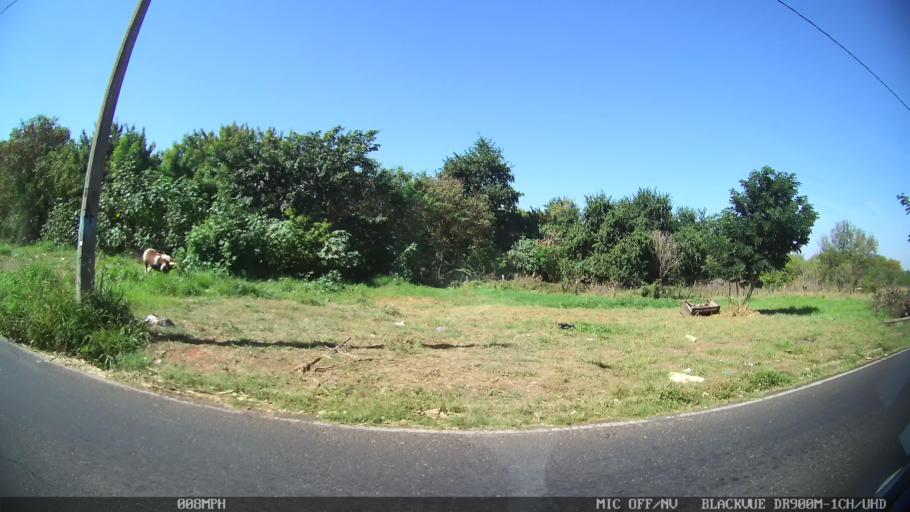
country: BR
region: Sao Paulo
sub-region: Sao Jose Do Rio Preto
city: Sao Jose do Rio Preto
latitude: -20.7705
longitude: -49.3988
